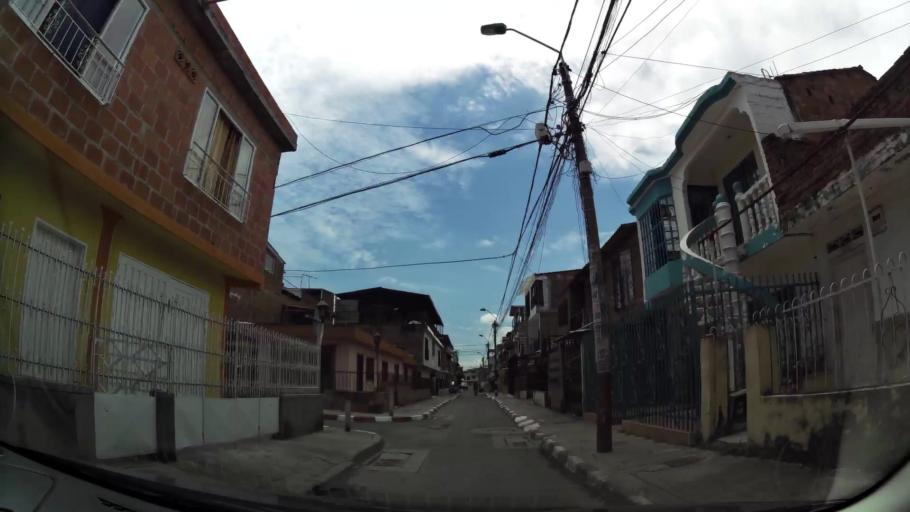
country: CO
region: Valle del Cauca
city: Cali
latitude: 3.4478
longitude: -76.4878
